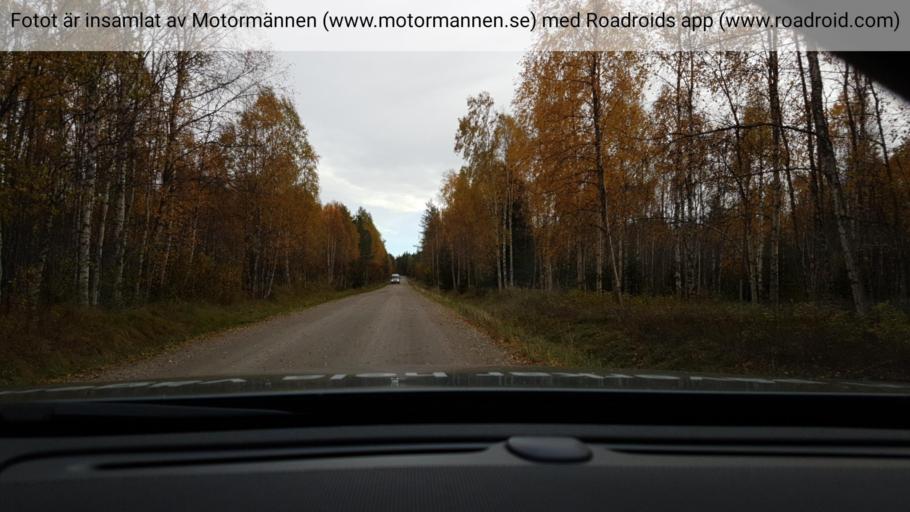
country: SE
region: Norrbotten
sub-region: Overkalix Kommun
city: OEverkalix
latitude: 66.2947
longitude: 22.9464
